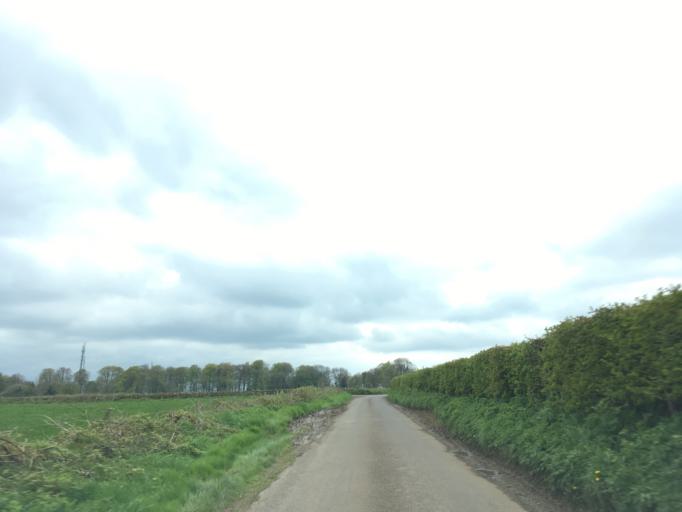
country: GB
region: England
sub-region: Gloucestershire
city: Wotton-under-Edge
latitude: 51.6637
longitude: -2.3002
